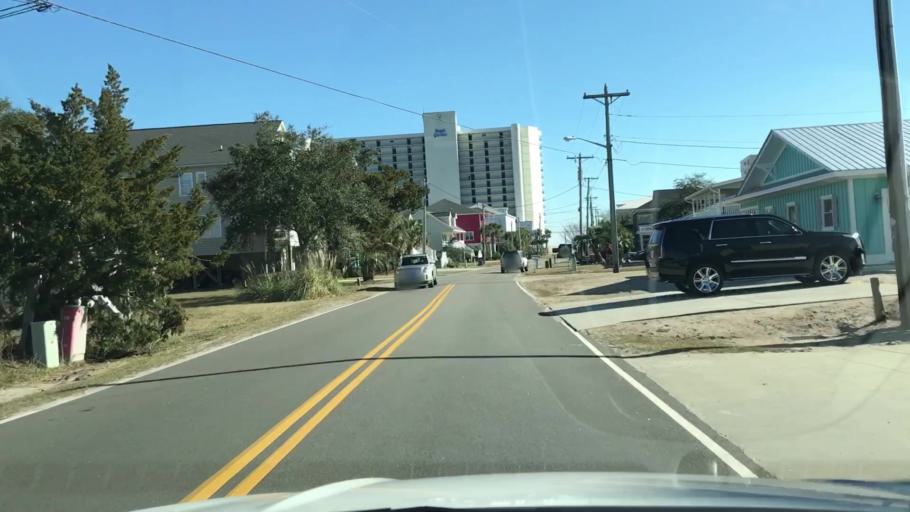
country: US
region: South Carolina
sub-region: Horry County
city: Garden City
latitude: 33.5870
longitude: -78.9928
